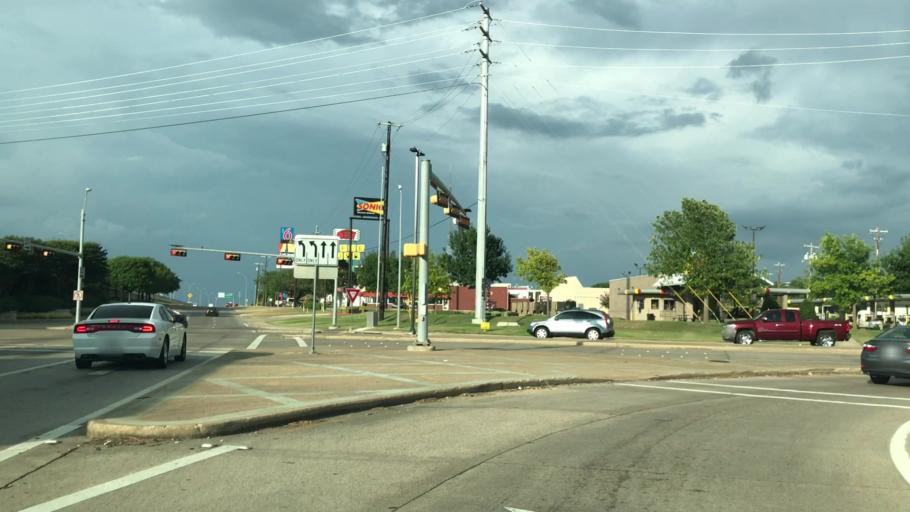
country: US
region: Texas
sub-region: Dallas County
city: Sunnyvale
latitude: 32.8376
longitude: -96.5965
